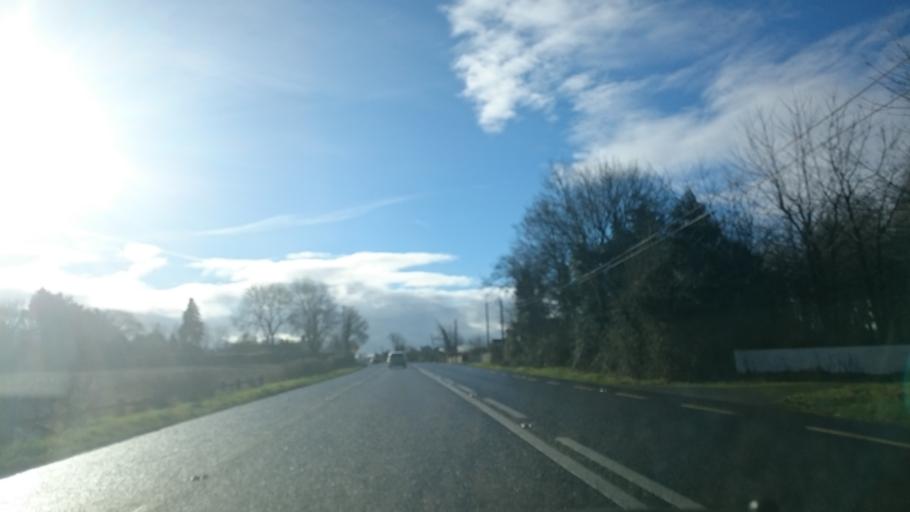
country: IE
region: Leinster
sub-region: Kilkenny
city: Kilkenny
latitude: 52.5983
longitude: -7.3050
